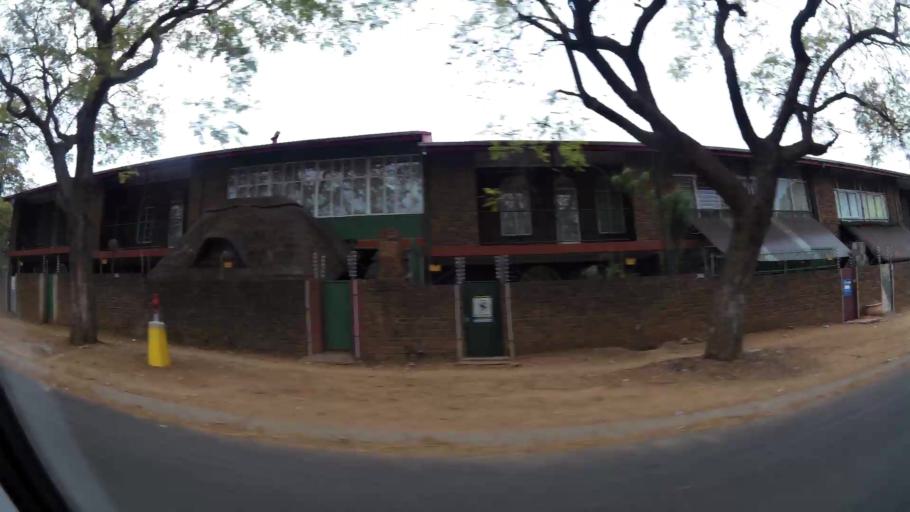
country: ZA
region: Limpopo
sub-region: Capricorn District Municipality
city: Polokwane
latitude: -23.9009
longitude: 29.4593
